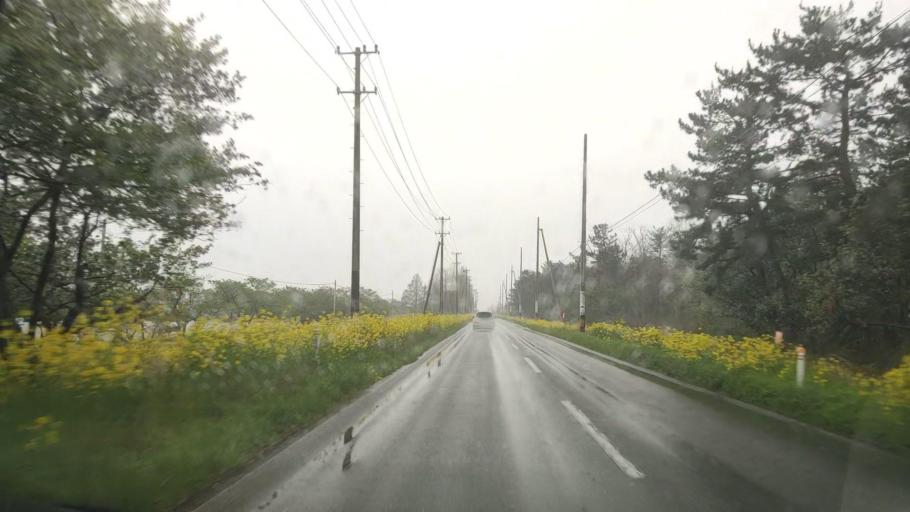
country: JP
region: Akita
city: Tenno
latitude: 40.0046
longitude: 139.9485
